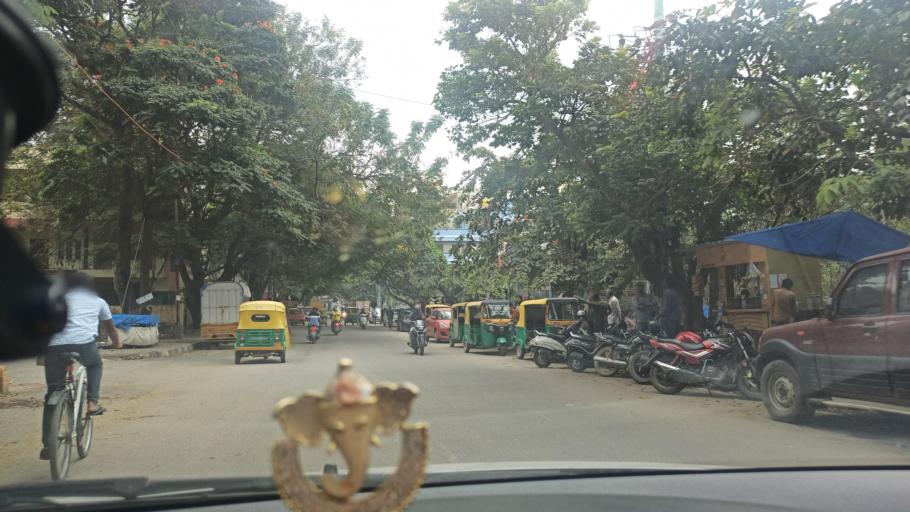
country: IN
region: Karnataka
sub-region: Bangalore Urban
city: Bangalore
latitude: 12.9159
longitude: 77.6491
